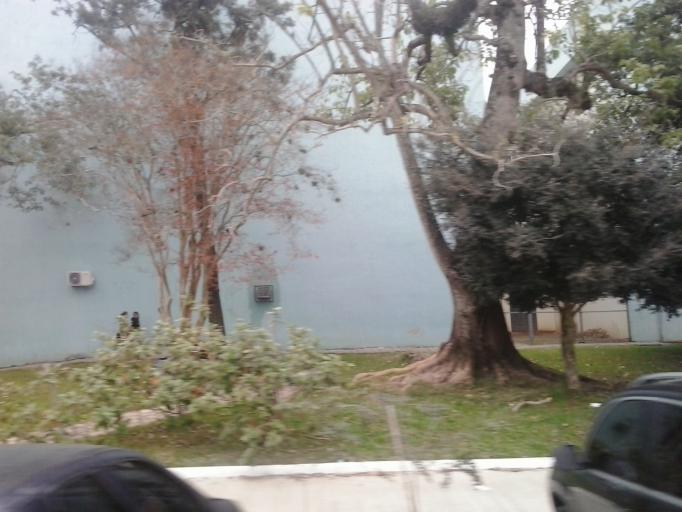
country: BR
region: Rio Grande do Sul
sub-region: Santa Maria
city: Santa Maria
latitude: -29.7140
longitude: -53.7167
